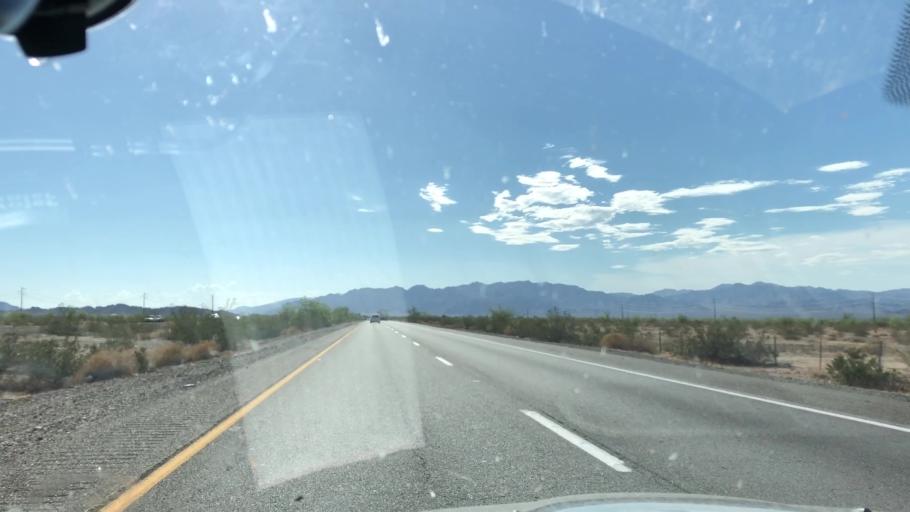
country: US
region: California
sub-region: Imperial County
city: Niland
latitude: 33.7078
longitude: -115.3563
